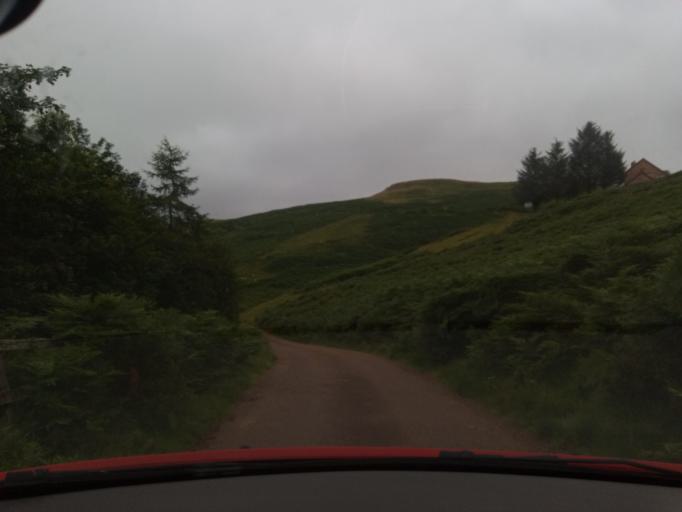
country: GB
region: England
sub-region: Northumberland
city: Rochester
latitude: 55.3699
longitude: -2.2146
